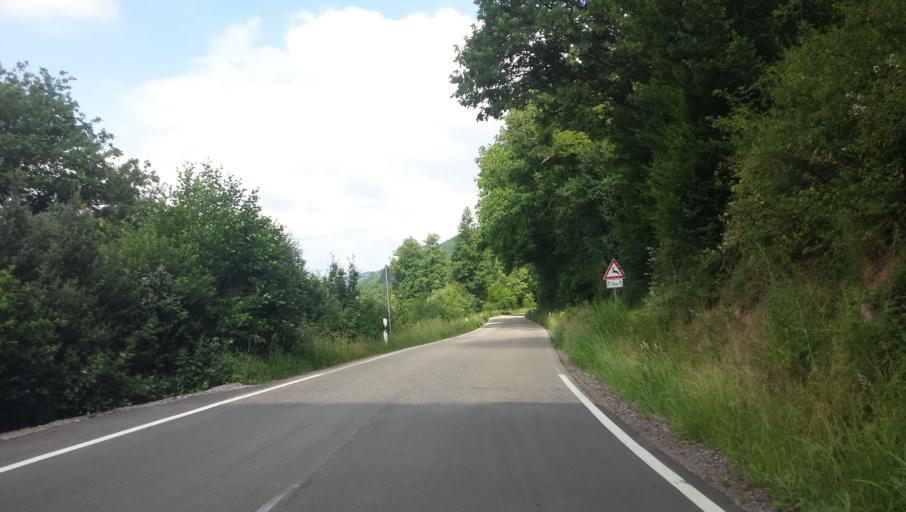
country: DE
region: Rheinland-Pfalz
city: Dernbach
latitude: 49.2318
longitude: 7.9983
